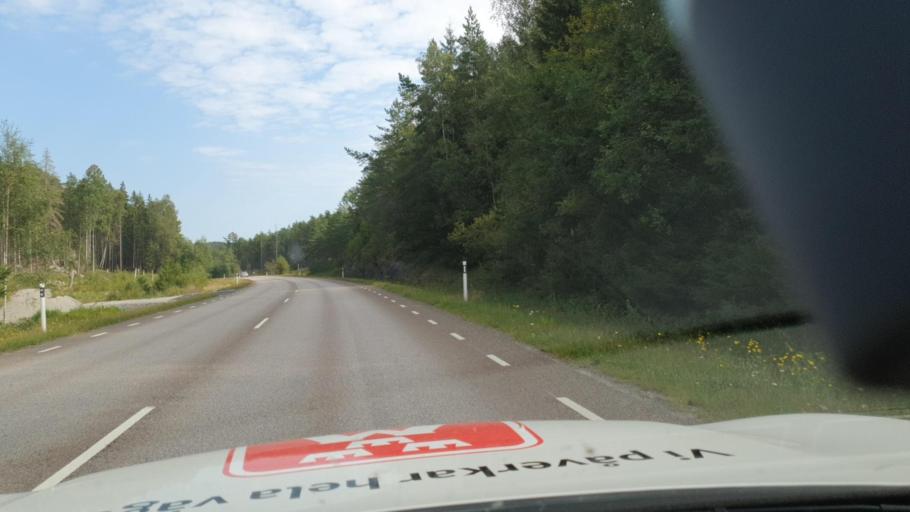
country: SE
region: Vaestra Goetaland
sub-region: Stromstads Kommun
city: Stroemstad
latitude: 59.0406
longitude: 11.2101
